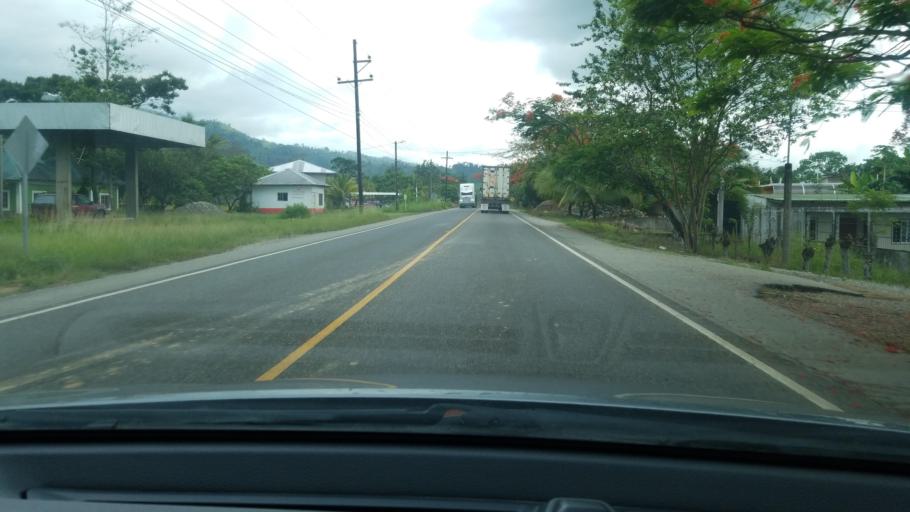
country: HN
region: Cortes
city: Potrerillos
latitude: 15.5939
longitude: -88.3227
